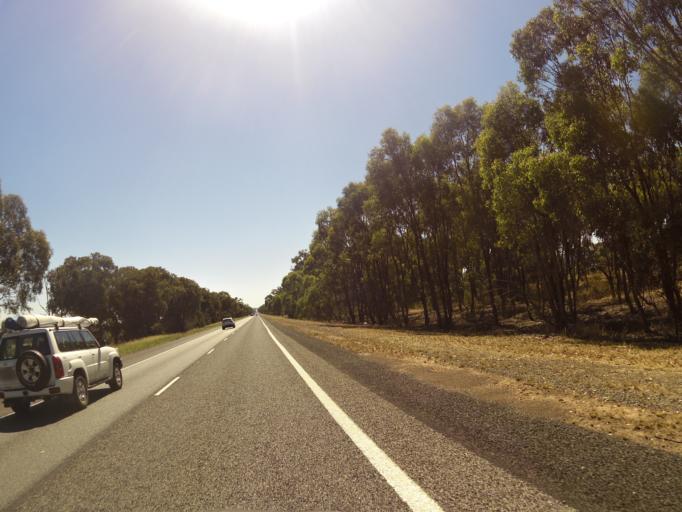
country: AU
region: Victoria
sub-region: Greater Shepparton
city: Shepparton
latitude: -36.8611
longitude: 145.3069
